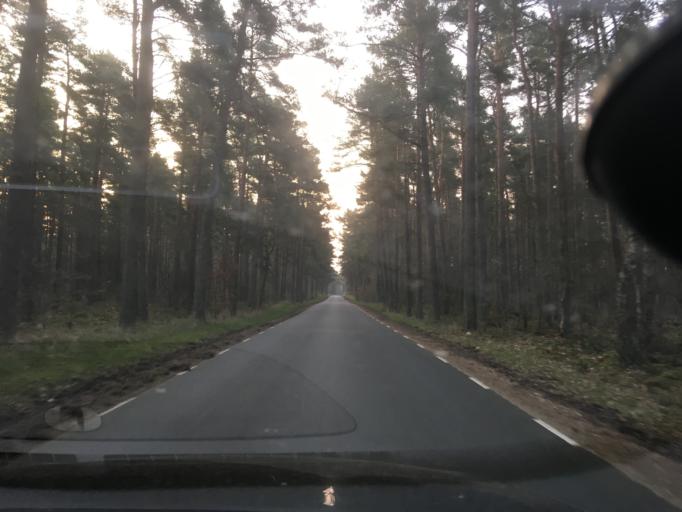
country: SE
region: Skane
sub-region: Simrishamns Kommun
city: Simrishamn
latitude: 55.3923
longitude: 14.1838
